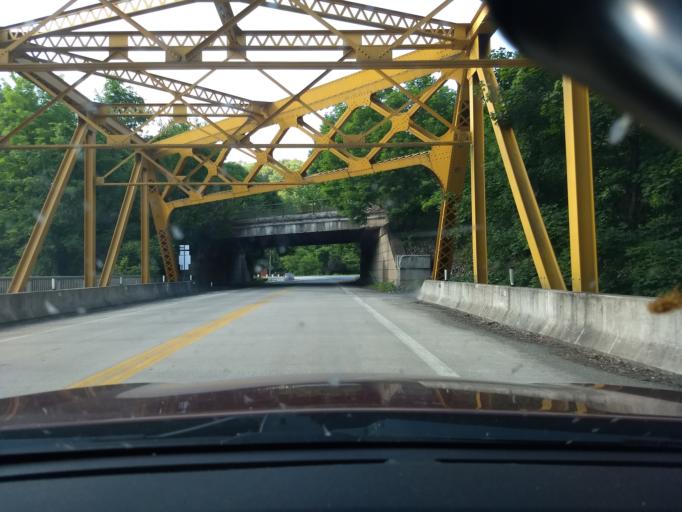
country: US
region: Pennsylvania
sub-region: Westmoreland County
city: Irwin
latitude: 40.3437
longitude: -79.7246
